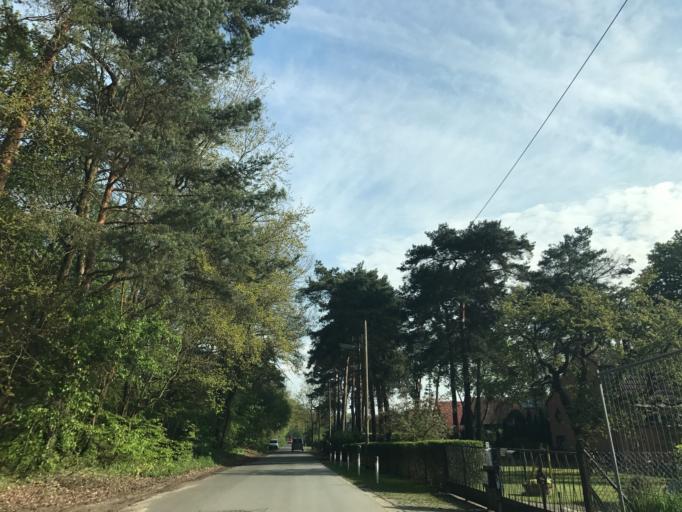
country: DE
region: Berlin
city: Staaken
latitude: 52.5242
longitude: 13.1279
